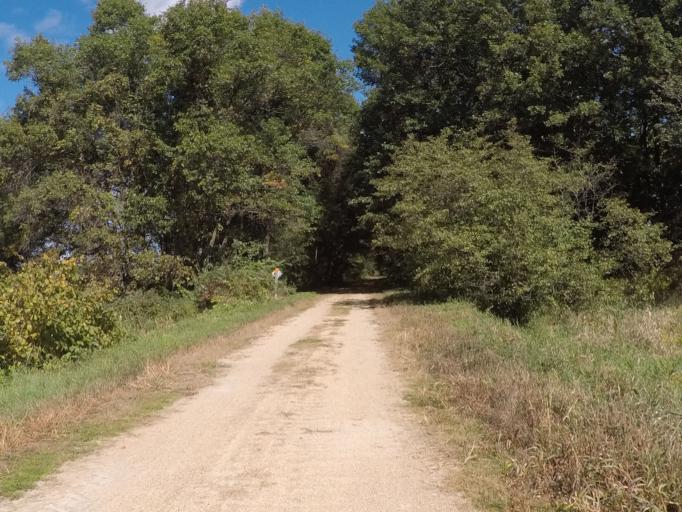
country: US
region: Wisconsin
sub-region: Richland County
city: Richland Center
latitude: 43.2463
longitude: -90.3051
